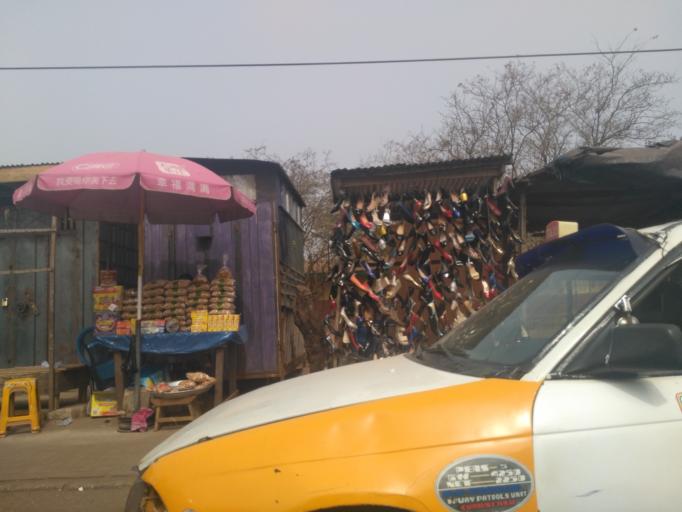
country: GH
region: Ashanti
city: Kumasi
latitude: 6.7076
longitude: -1.6367
